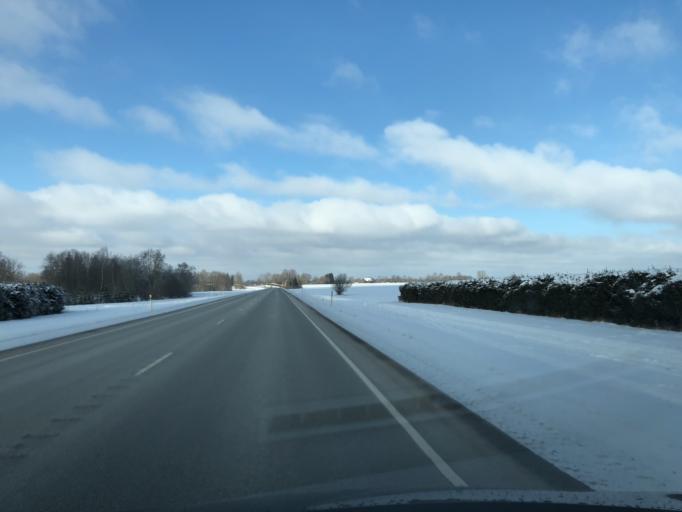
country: EE
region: Jaervamaa
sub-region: Paide linn
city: Paide
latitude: 58.8571
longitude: 25.7201
